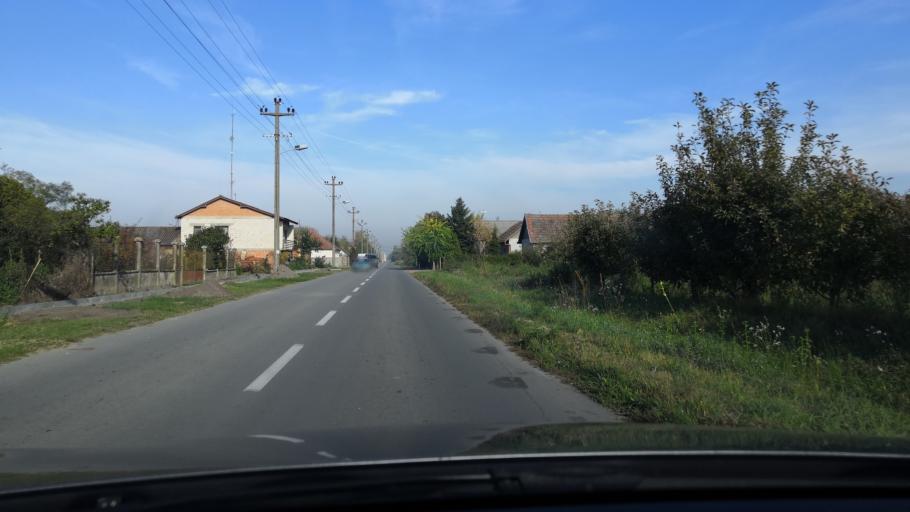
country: HU
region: Csongrad
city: Morahalom
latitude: 46.1298
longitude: 19.8561
